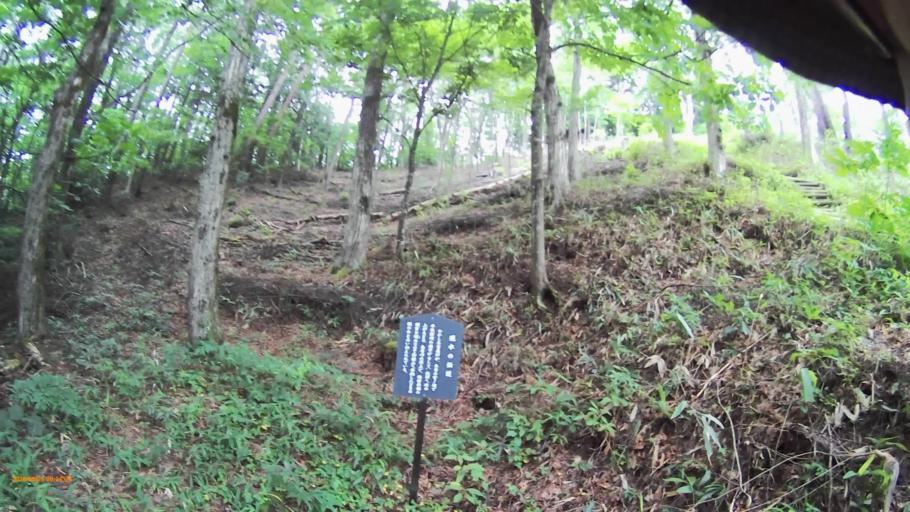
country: JP
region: Nagano
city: Ina
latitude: 35.9493
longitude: 137.7927
